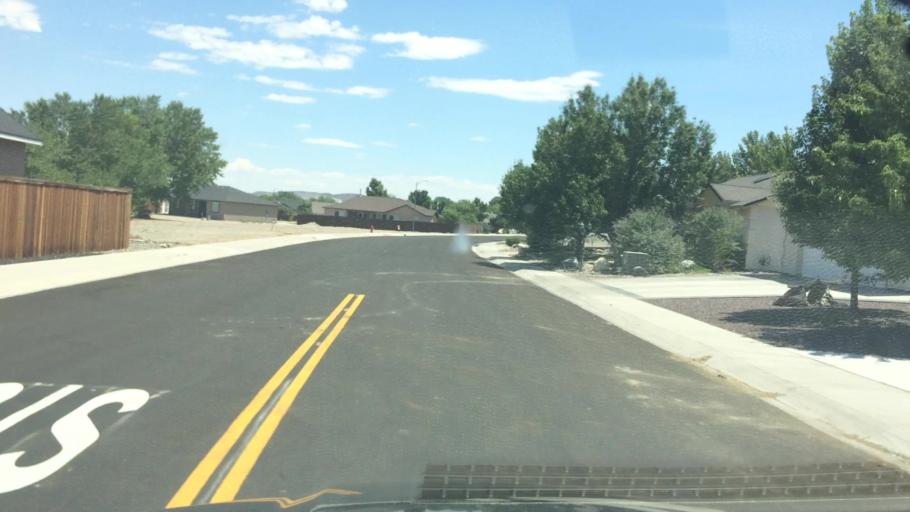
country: US
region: Nevada
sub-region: Lyon County
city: Fernley
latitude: 39.5842
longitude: -119.1443
